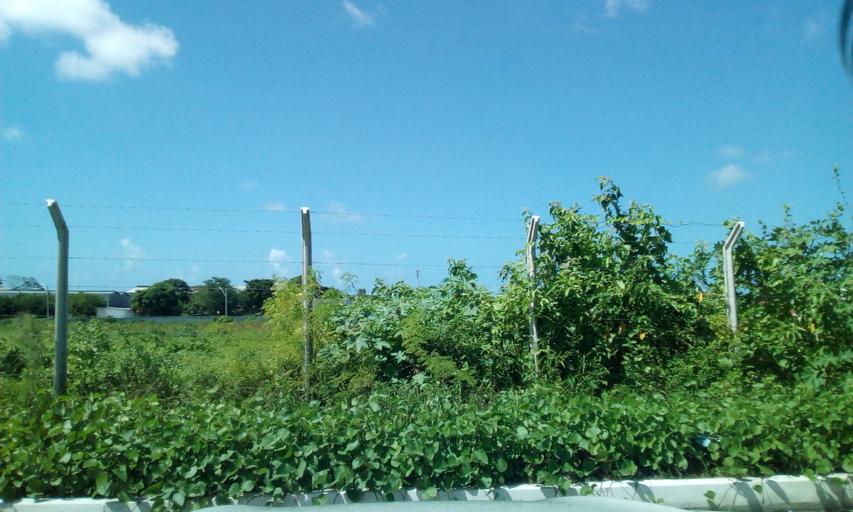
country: BR
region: Paraiba
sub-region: Joao Pessoa
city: Joao Pessoa
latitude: -7.1728
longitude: -34.8685
